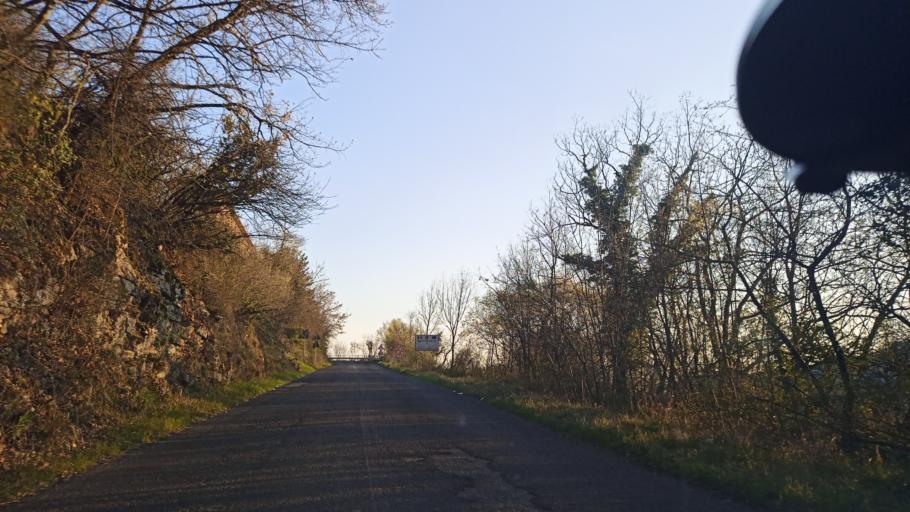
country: IT
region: Latium
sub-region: Provincia di Rieti
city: Cottanello
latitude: 42.4113
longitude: 12.6844
